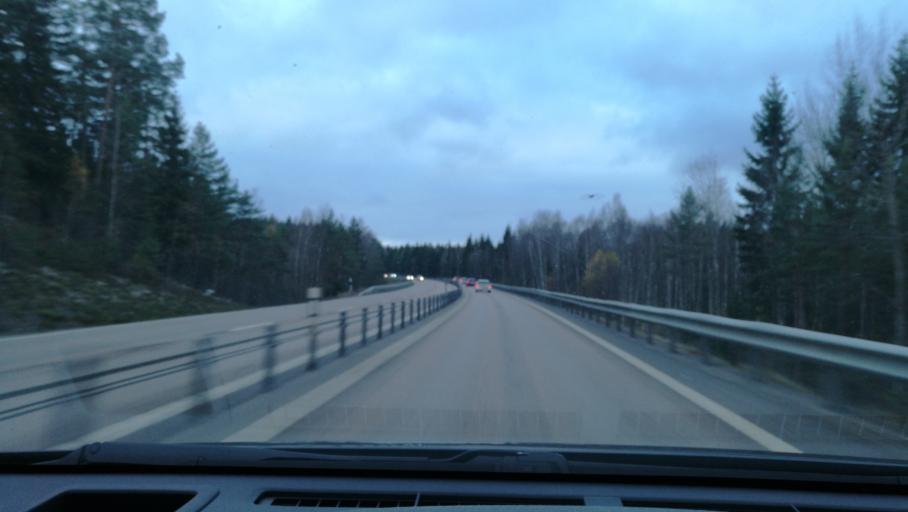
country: SE
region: Soedermanland
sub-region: Eskilstuna Kommun
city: Kvicksund
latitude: 59.4170
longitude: 16.3653
